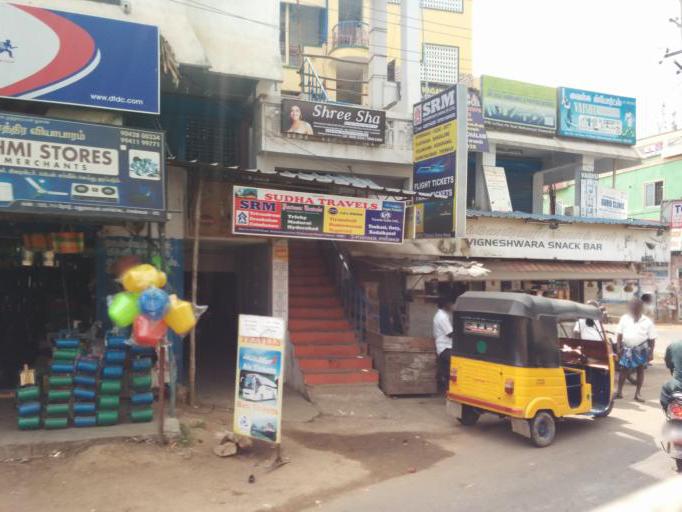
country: IN
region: Tamil Nadu
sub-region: Thiruvallur
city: Porur
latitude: 13.0638
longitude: 80.1680
